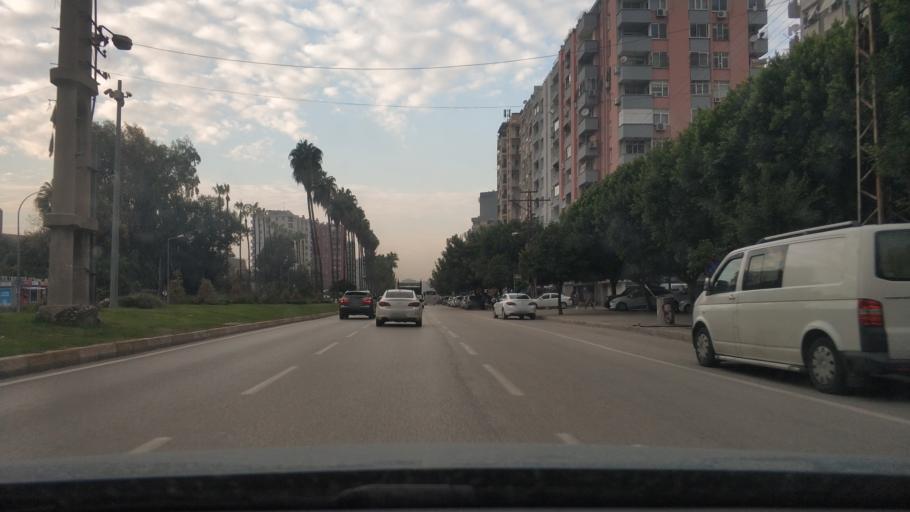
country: TR
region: Adana
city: Adana
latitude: 36.9999
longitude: 35.3160
